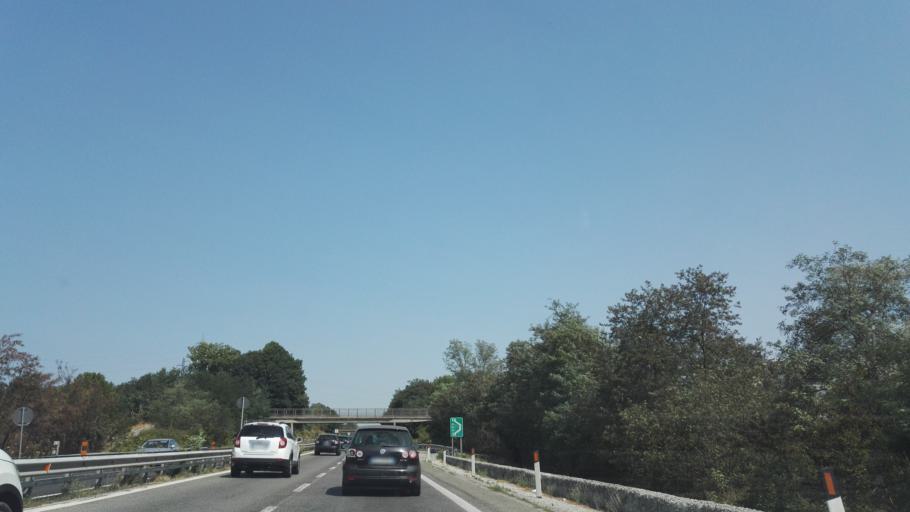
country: IT
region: Calabria
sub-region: Provincia di Cosenza
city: Santo Stefano di Rogliano
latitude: 39.2072
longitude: 16.3092
